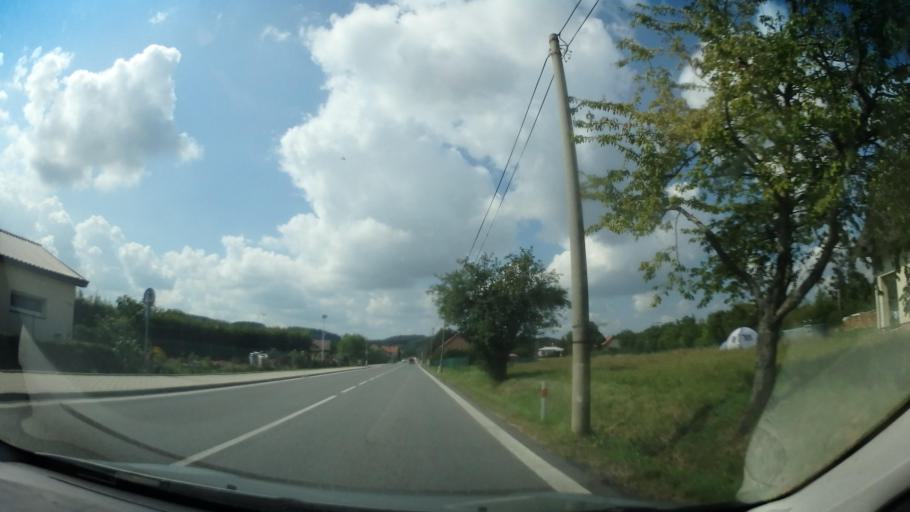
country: CZ
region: Central Bohemia
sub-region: Okres Kolin
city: Kourim
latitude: 49.9668
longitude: 14.9638
